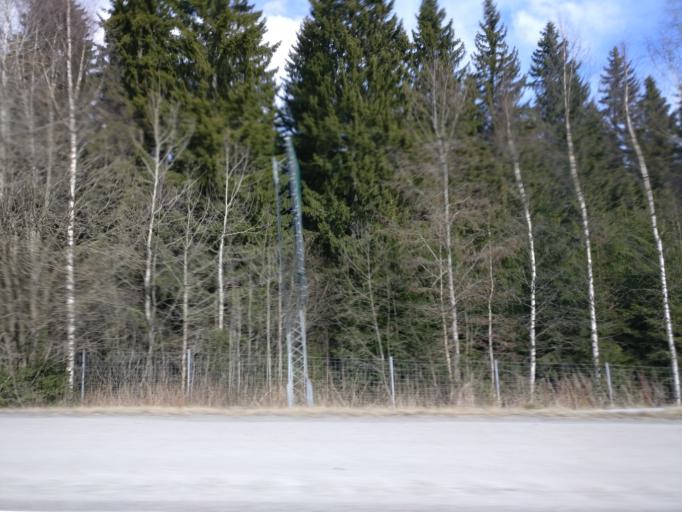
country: FI
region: Haeme
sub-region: Haemeenlinna
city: Haemeenlinna
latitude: 60.9530
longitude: 24.4949
